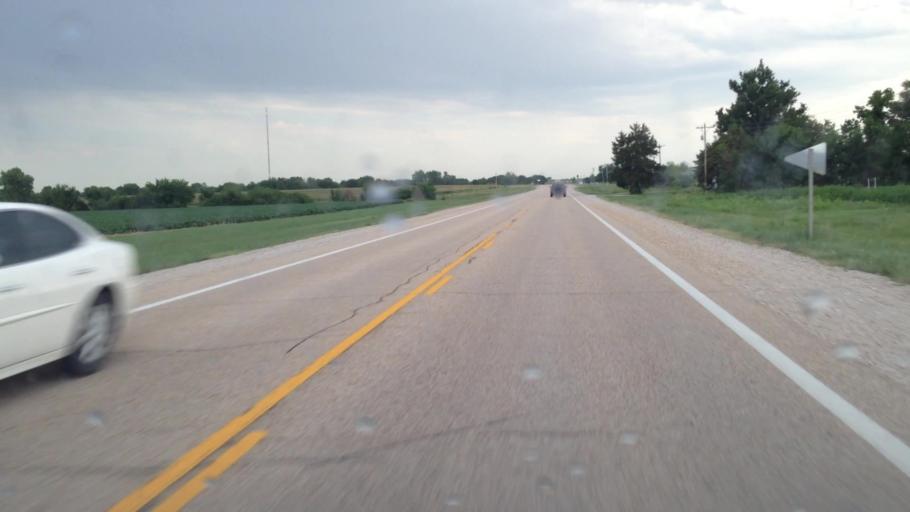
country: US
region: Kansas
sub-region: Coffey County
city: Burlington
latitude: 38.1752
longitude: -95.7389
